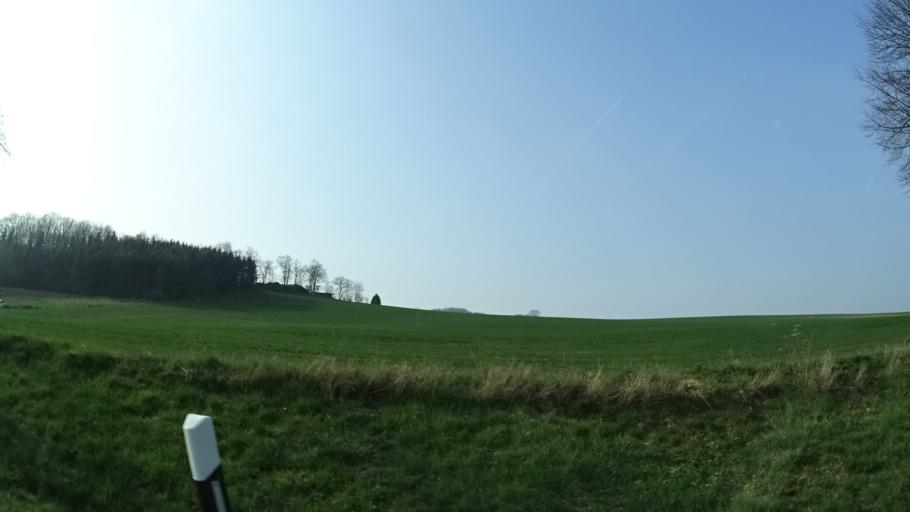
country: DE
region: Rheinland-Pfalz
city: Oberstaufenbach
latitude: 49.5217
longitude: 7.5097
